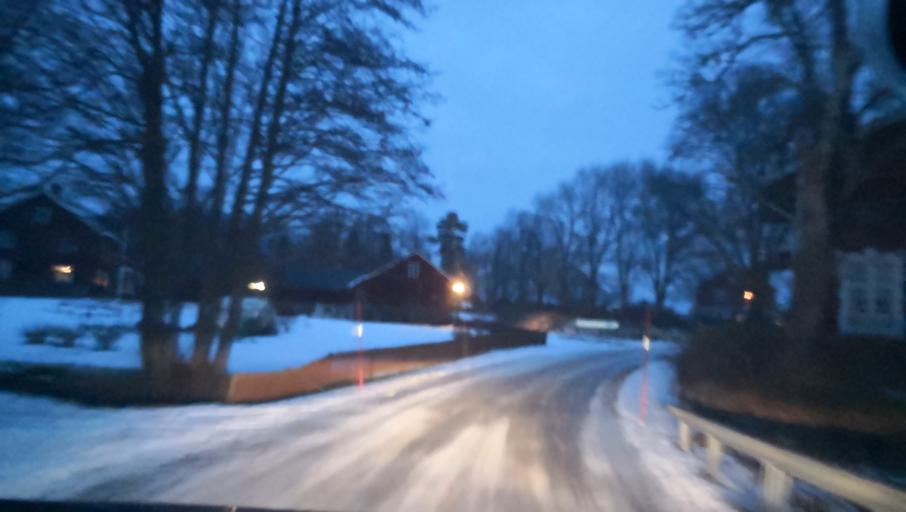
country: SE
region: Uppsala
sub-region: Heby Kommun
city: Tarnsjo
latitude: 60.2440
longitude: 16.6835
